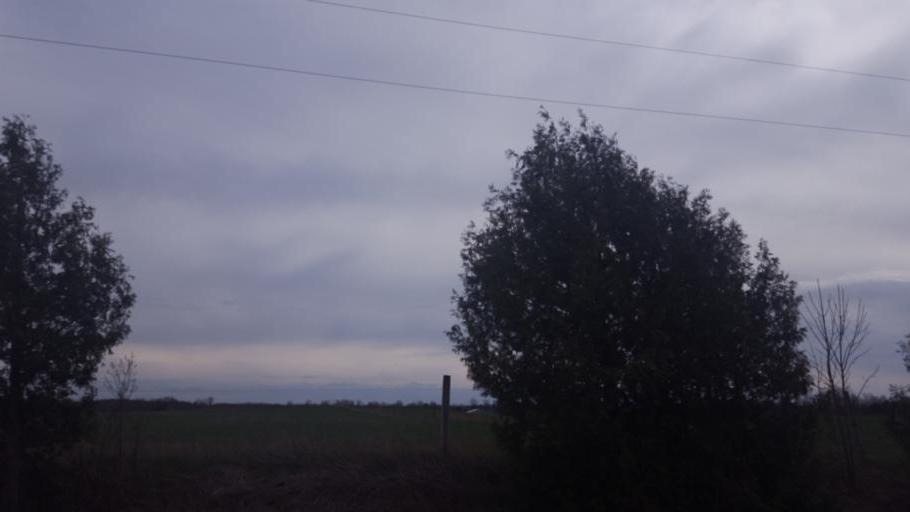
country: US
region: Michigan
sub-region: Clare County
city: Clare
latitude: 43.8729
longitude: -84.7449
